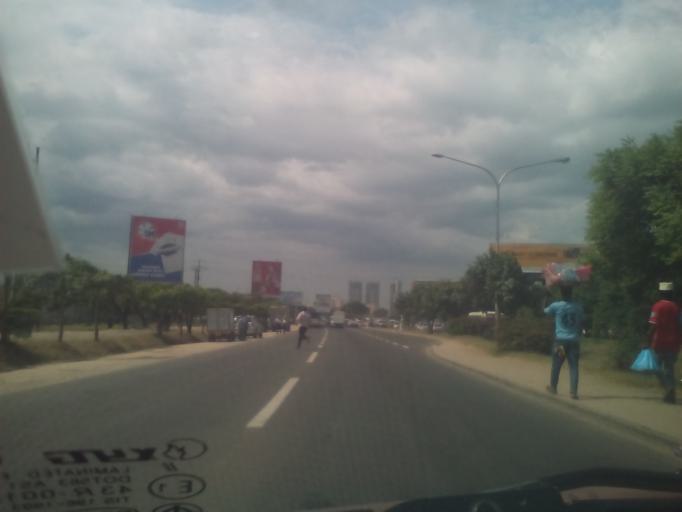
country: TZ
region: Dar es Salaam
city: Dar es Salaam
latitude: -6.8329
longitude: 39.2674
